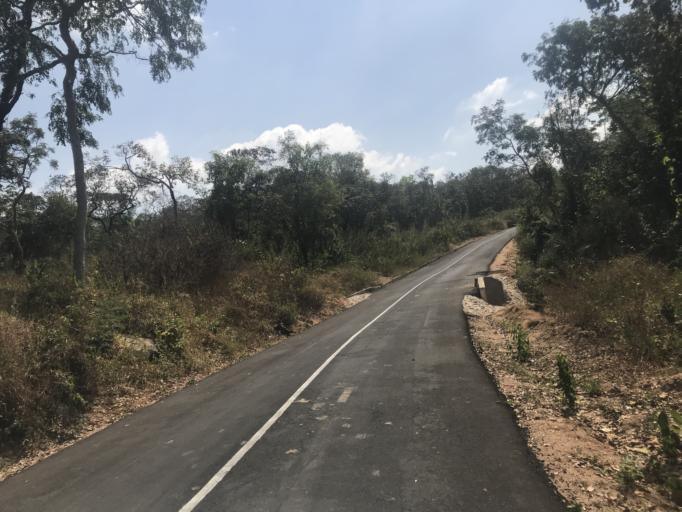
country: NG
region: Osun
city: Otan Ayegbaju
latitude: 7.8975
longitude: 4.8354
